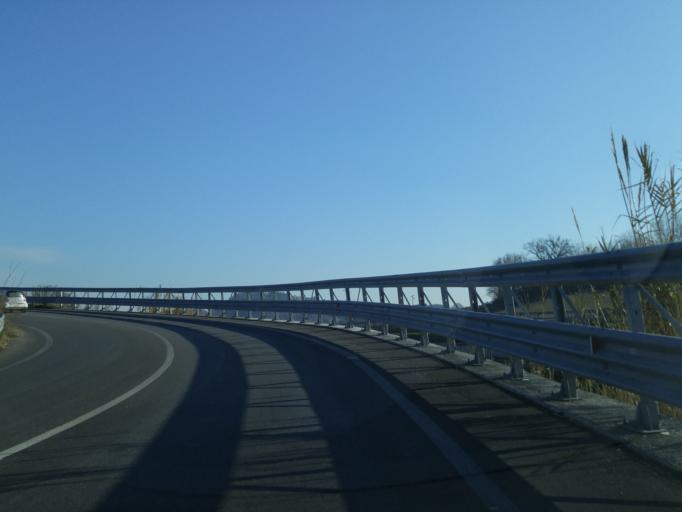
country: IT
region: The Marches
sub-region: Provincia di Pesaro e Urbino
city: Fanano
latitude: 43.9525
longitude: 12.7545
